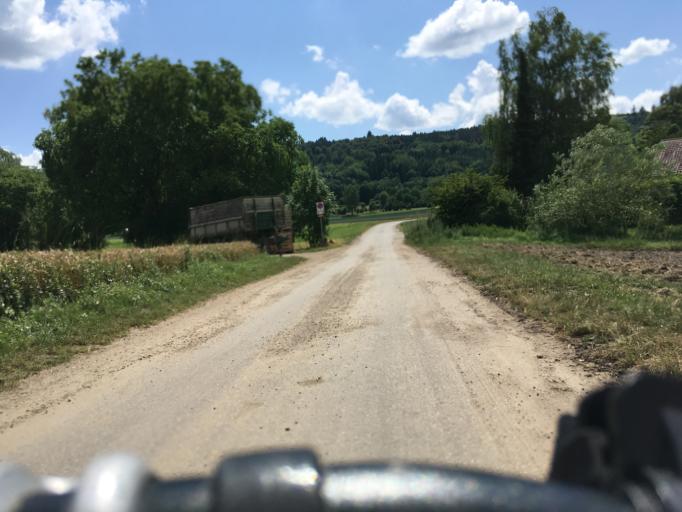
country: DE
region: Baden-Wuerttemberg
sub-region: Freiburg Region
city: Busingen
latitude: 47.6844
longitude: 8.6819
